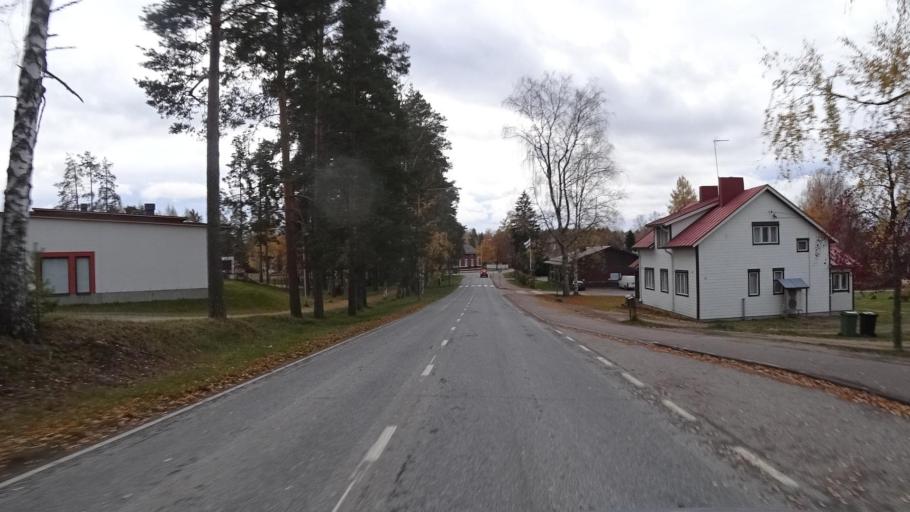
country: FI
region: Central Finland
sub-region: Joutsa
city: Joutsa
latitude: 61.7465
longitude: 26.1209
